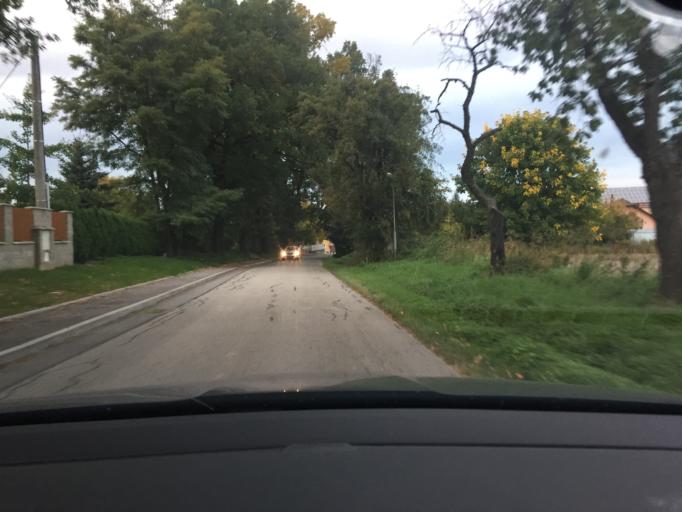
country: CZ
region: Jihocesky
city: Netolice
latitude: 49.0301
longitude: 14.2712
